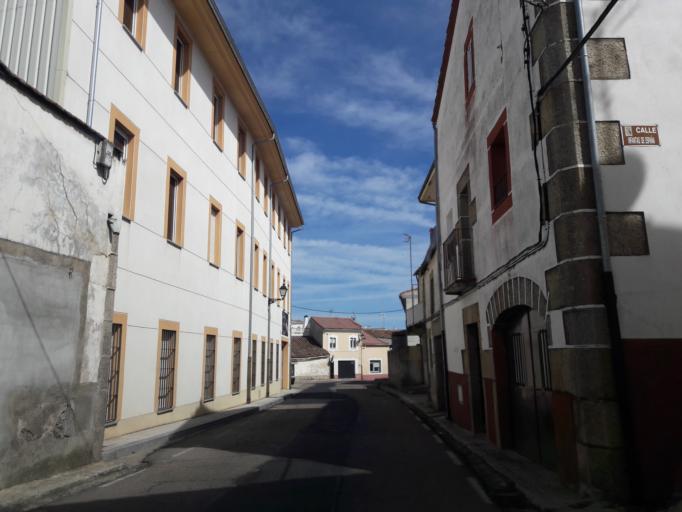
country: ES
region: Castille and Leon
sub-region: Provincia de Salamanca
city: Ledrada
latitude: 40.4679
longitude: -5.7209
